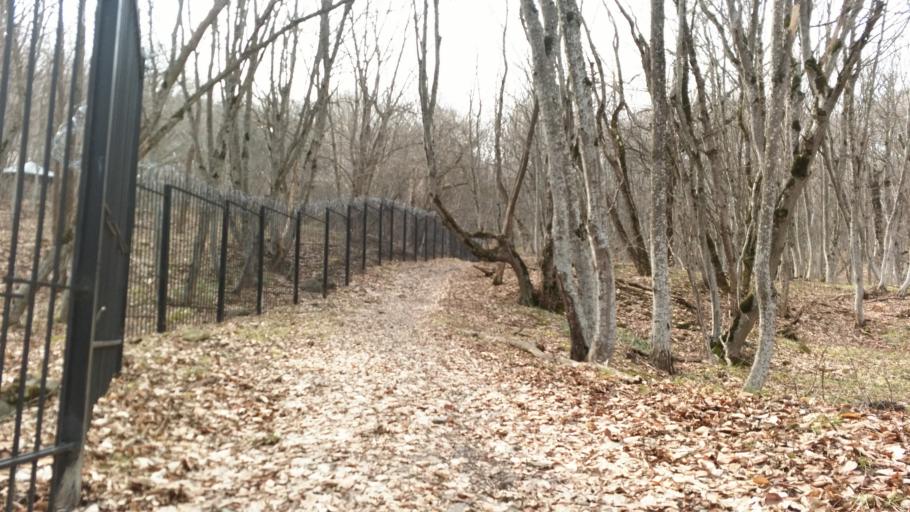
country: RU
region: Stavropol'skiy
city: Zheleznovodsk
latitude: 44.1293
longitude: 43.0246
